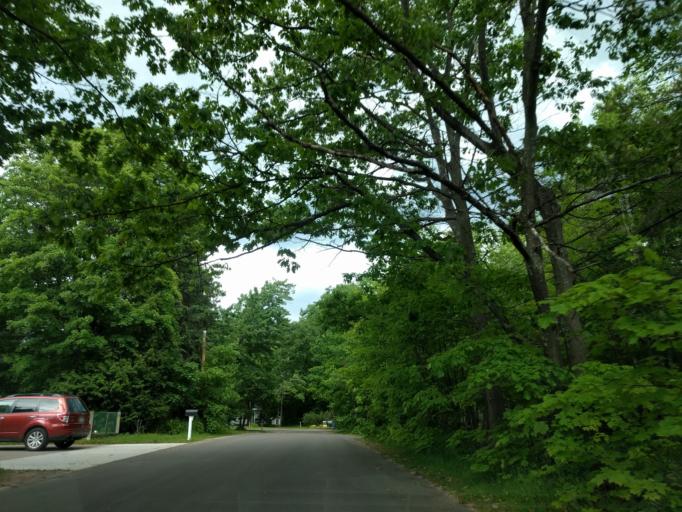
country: US
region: Michigan
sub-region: Marquette County
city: Trowbridge Park
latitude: 46.5626
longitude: -87.4399
